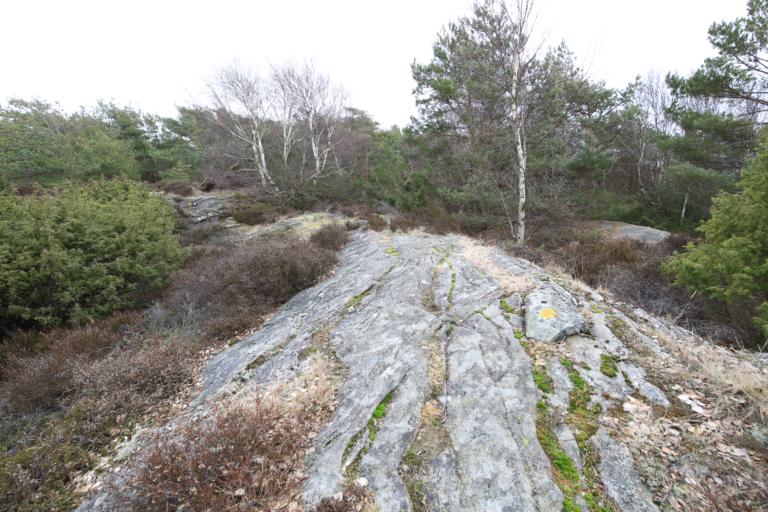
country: SE
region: Halland
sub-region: Kungsbacka Kommun
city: Frillesas
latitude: 57.2360
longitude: 12.0995
